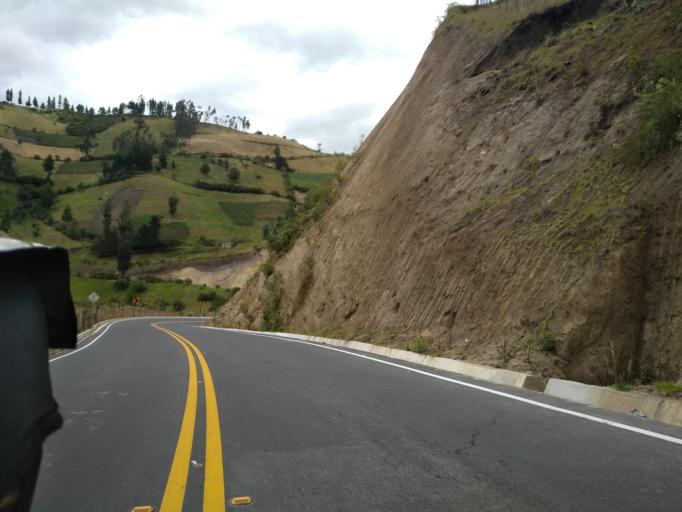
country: EC
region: Cotopaxi
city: Saquisili
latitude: -0.7271
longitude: -78.8996
